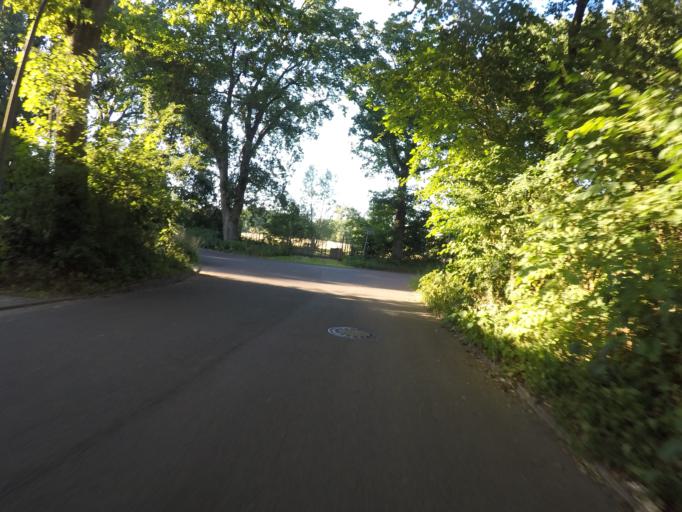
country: DE
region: Hamburg
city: Bergstedt
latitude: 53.6729
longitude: 10.1113
